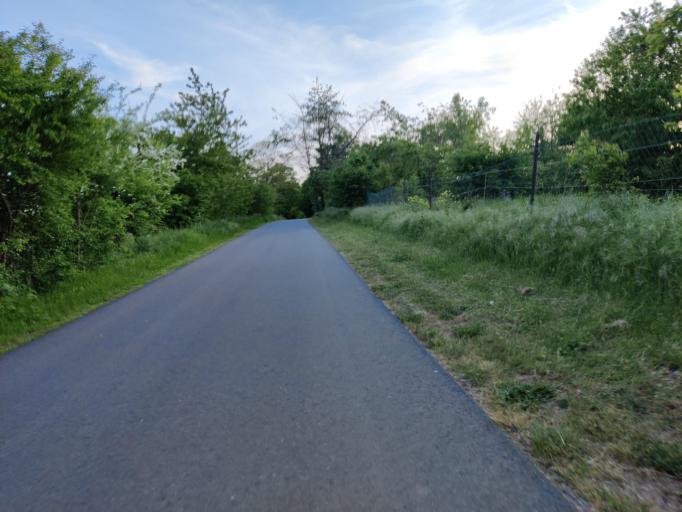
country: DE
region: Saxony-Anhalt
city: Karsdorf
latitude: 51.2480
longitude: 11.6463
